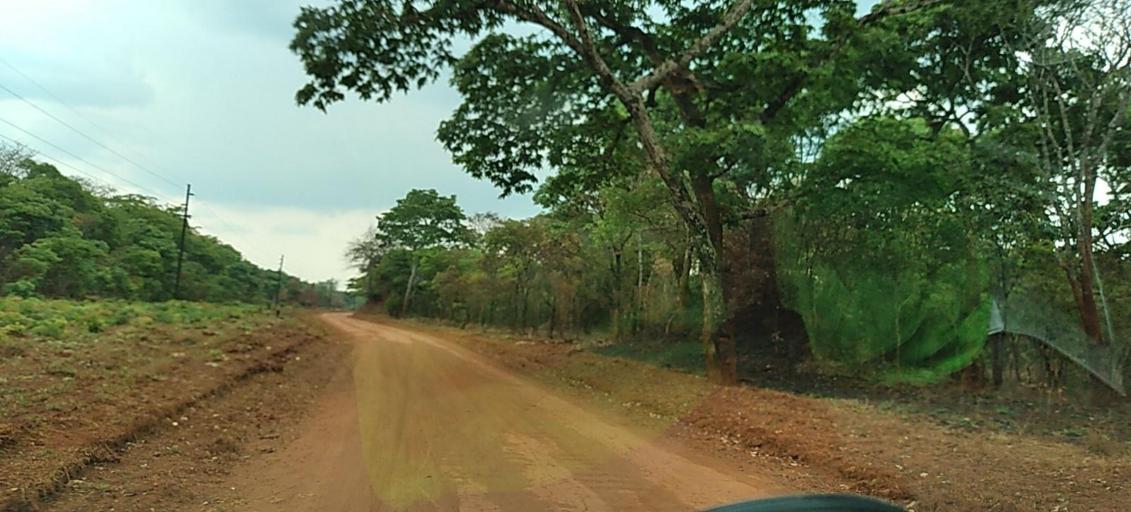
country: ZM
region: North-Western
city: Solwezi
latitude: -12.7811
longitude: 26.4848
